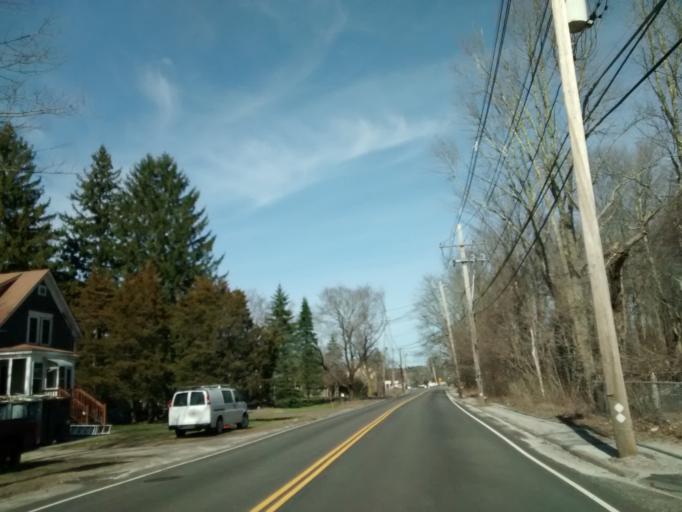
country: US
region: Massachusetts
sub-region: Norfolk County
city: Bellingham
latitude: 42.1312
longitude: -71.4496
